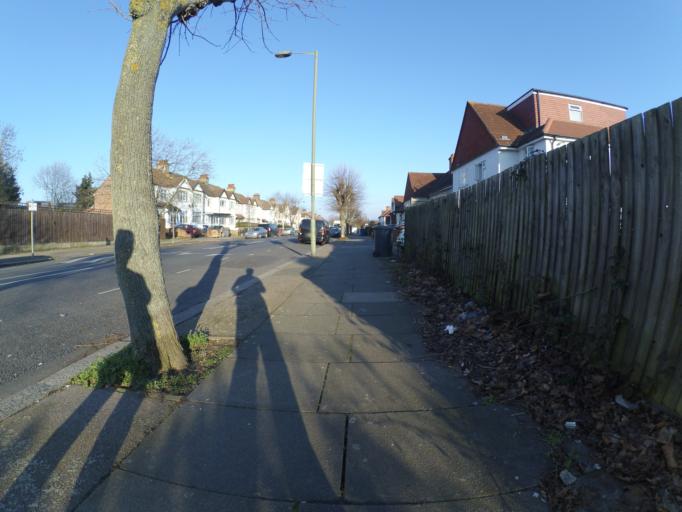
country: GB
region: England
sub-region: Greater London
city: Hendon
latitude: 51.5776
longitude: -0.2315
